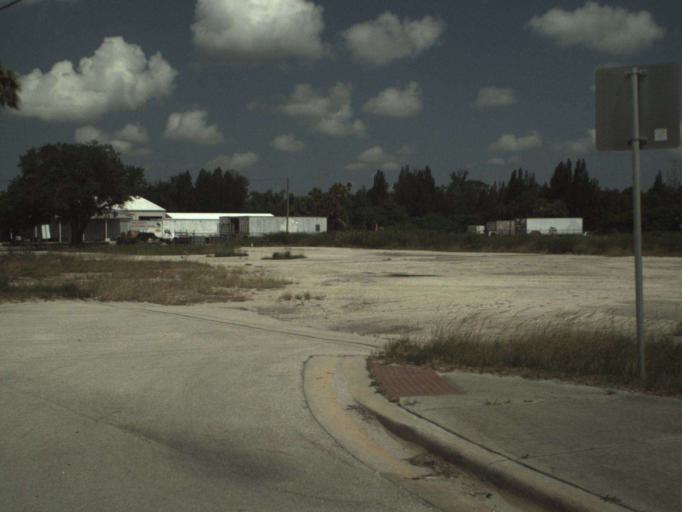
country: US
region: Florida
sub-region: Saint Lucie County
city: Lakewood Park
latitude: 27.4476
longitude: -80.3857
